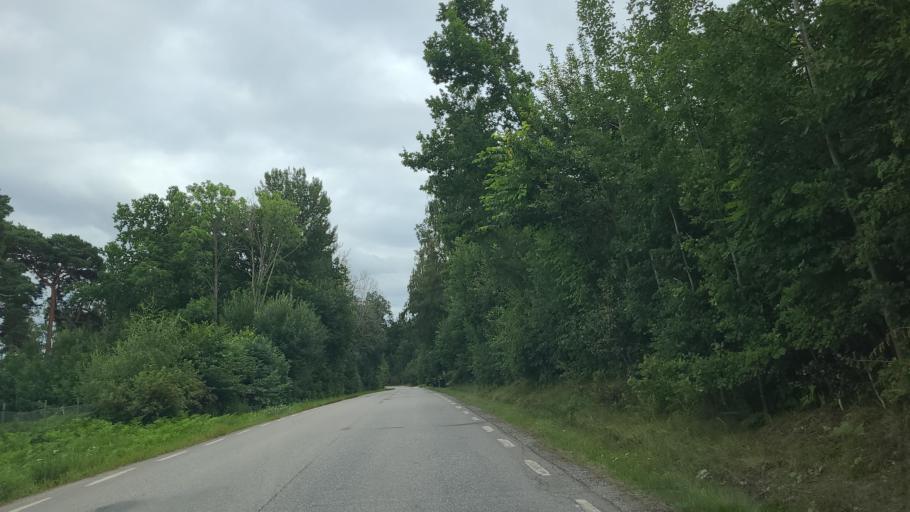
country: SE
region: Stockholm
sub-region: Upplands-Bro Kommun
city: Bro
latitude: 59.4989
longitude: 17.5677
